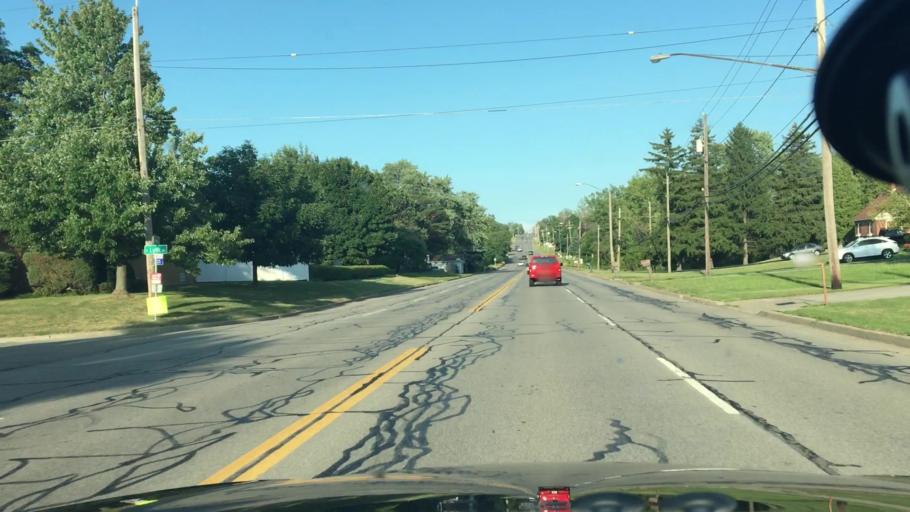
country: US
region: New York
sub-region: Erie County
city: Blasdell
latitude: 42.7968
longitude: -78.8070
